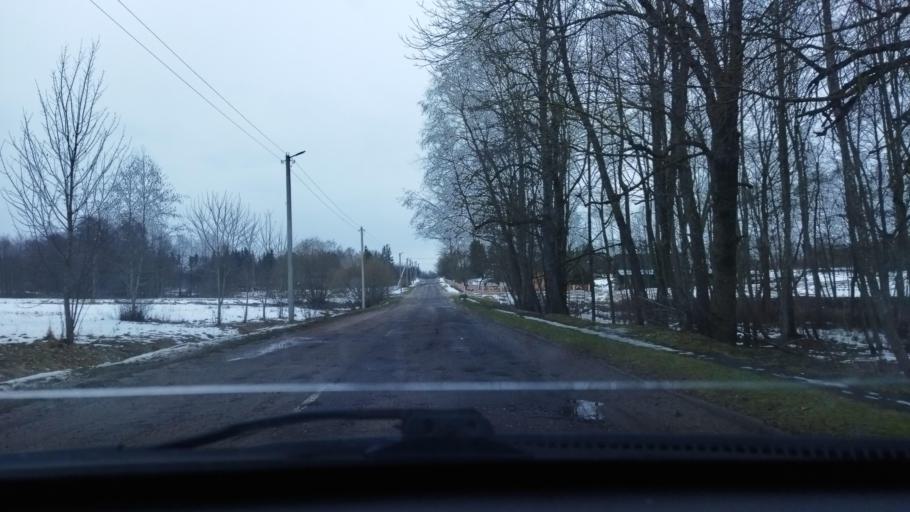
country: BY
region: Minsk
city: Svir
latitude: 54.8995
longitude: 26.4020
